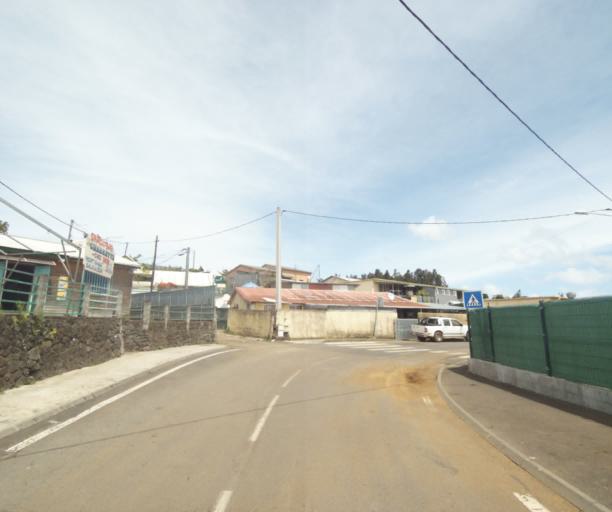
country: RE
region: Reunion
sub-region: Reunion
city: Trois-Bassins
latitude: -21.0664
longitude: 55.3081
